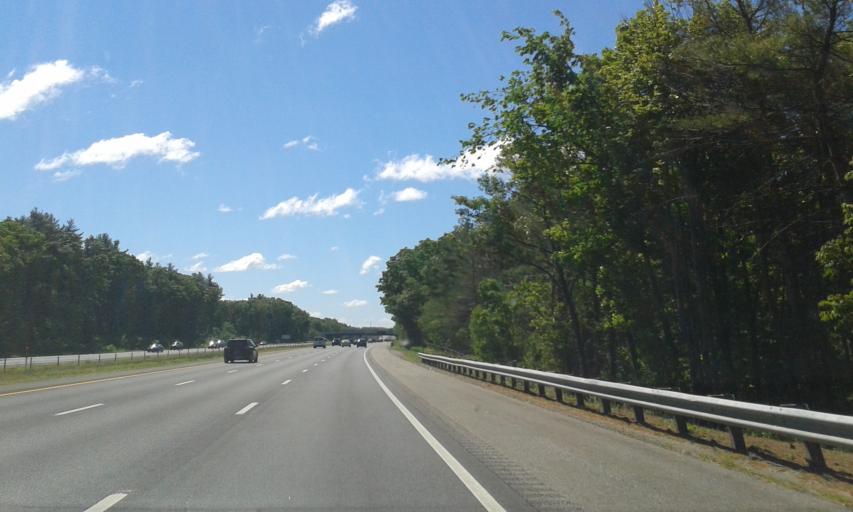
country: US
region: Massachusetts
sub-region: Middlesex County
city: Bedford
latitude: 42.5234
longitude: -71.2652
